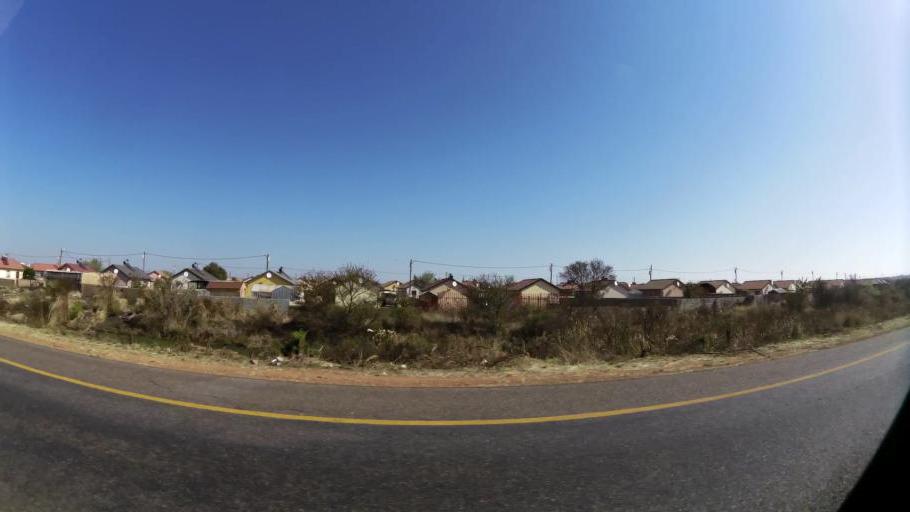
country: ZA
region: Gauteng
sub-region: City of Tshwane Metropolitan Municipality
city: Mabopane
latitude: -25.6025
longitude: 28.1137
